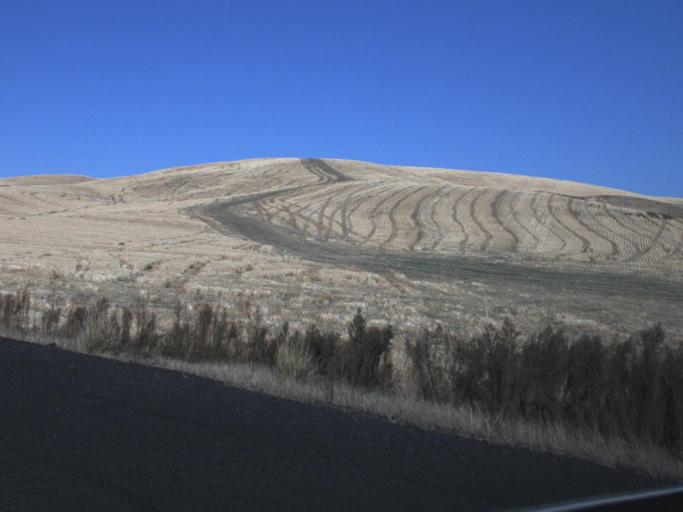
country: US
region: Washington
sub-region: Adams County
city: Ritzville
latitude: 46.7832
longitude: -118.2872
